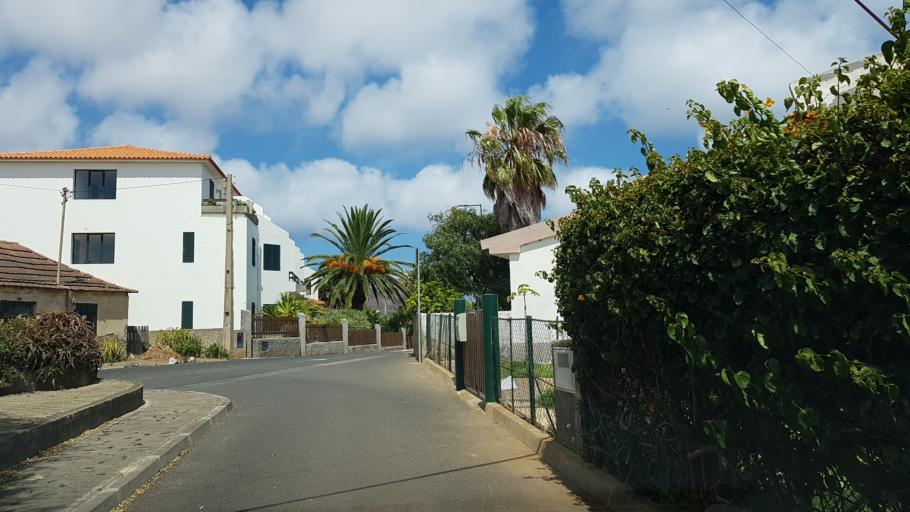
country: PT
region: Madeira
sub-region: Porto Santo
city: Vila de Porto Santo
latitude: 33.0593
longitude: -16.3382
